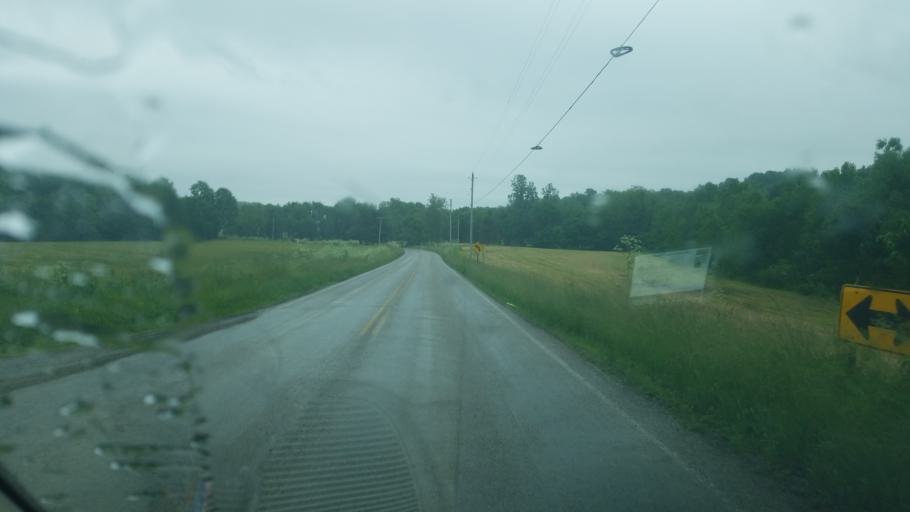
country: US
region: Ohio
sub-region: Sandusky County
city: Bellville
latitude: 40.6803
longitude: -82.4544
